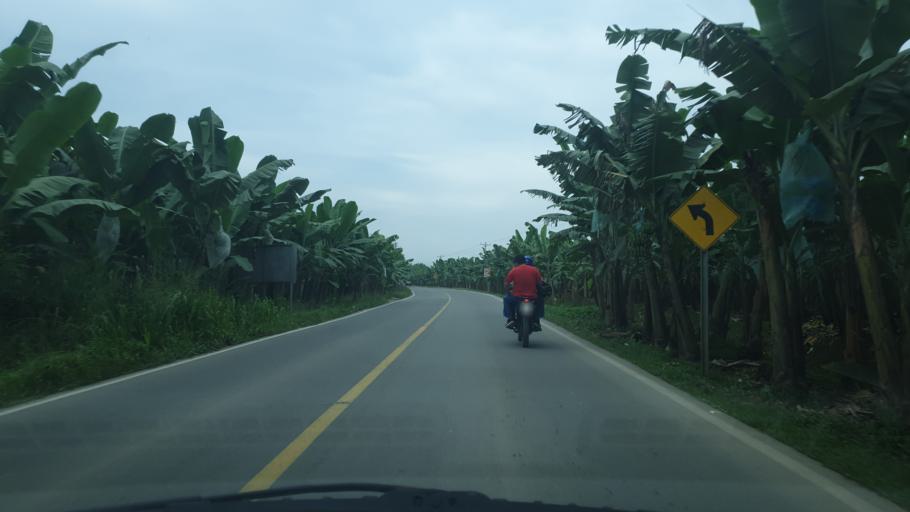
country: EC
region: El Oro
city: Pasaje
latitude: -3.3621
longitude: -79.8387
